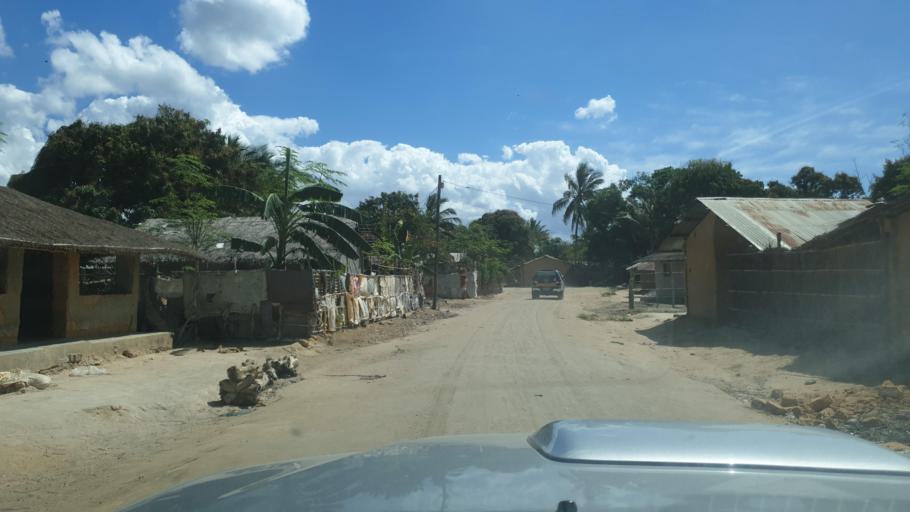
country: MZ
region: Nampula
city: Nacala
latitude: -14.5711
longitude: 40.6889
